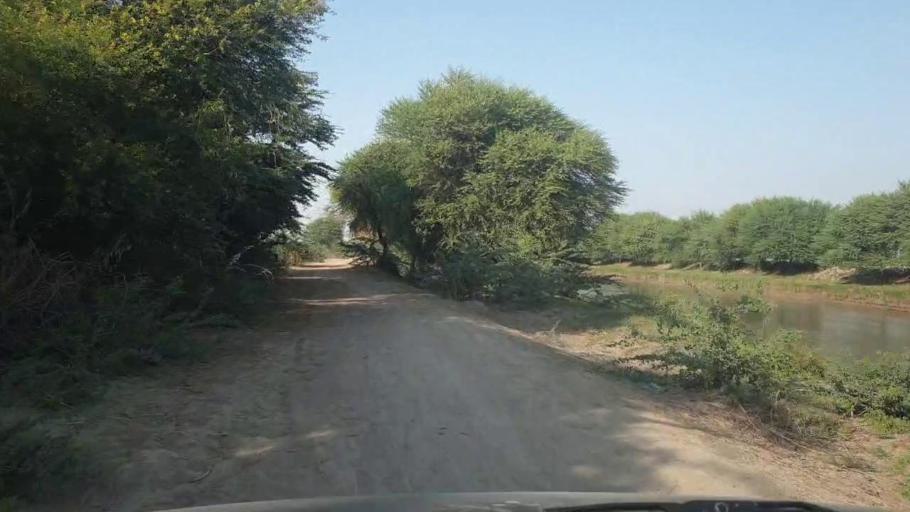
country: PK
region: Sindh
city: Badin
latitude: 24.6407
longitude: 68.8151
